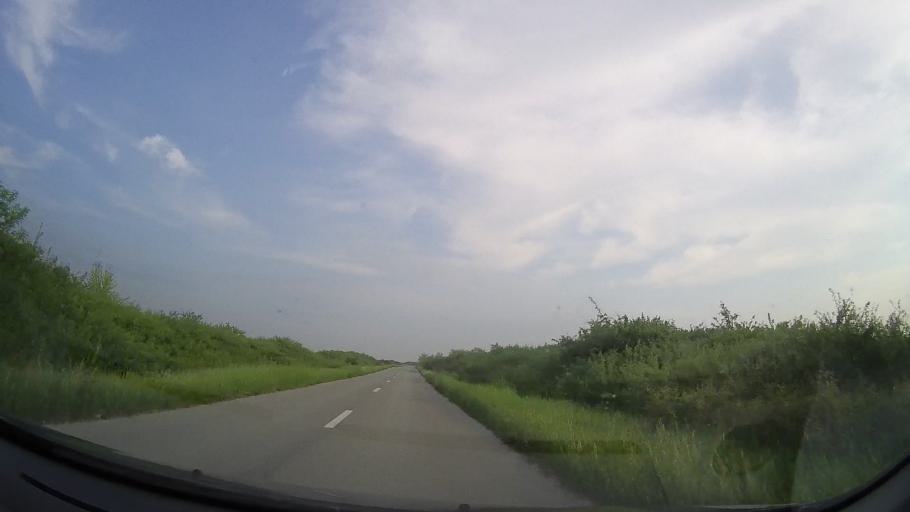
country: RS
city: Jasa Tomic
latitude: 45.4770
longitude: 20.8471
